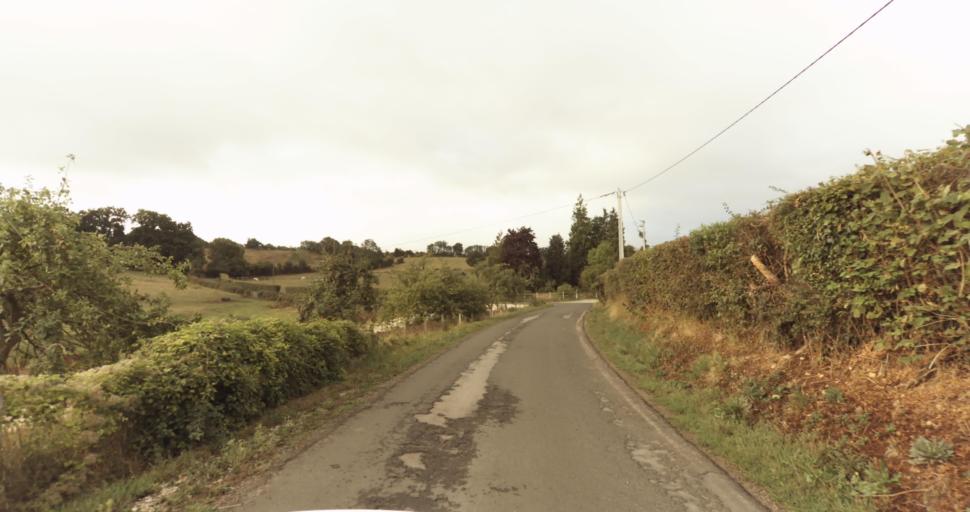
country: FR
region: Lower Normandy
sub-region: Departement de l'Orne
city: Trun
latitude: 48.9119
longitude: 0.1003
